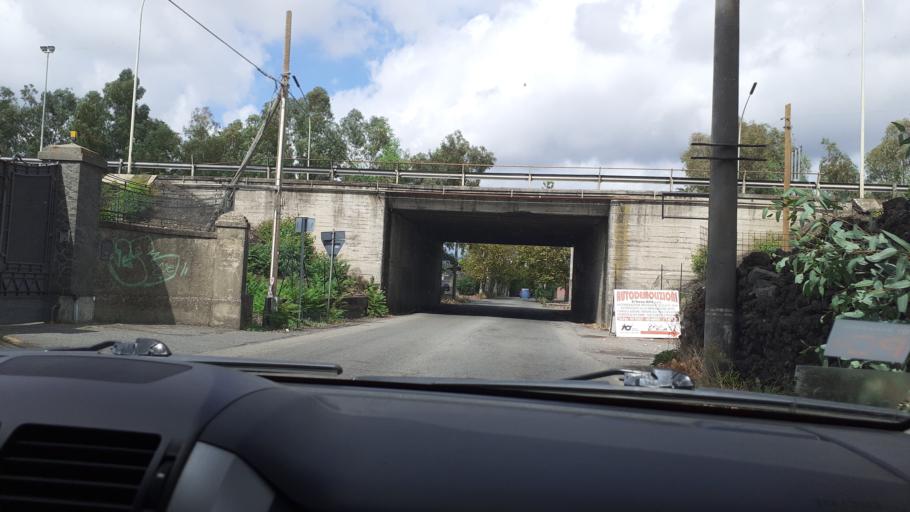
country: IT
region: Sicily
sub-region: Catania
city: San Gregorio di Catania
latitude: 37.5683
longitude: 15.1051
